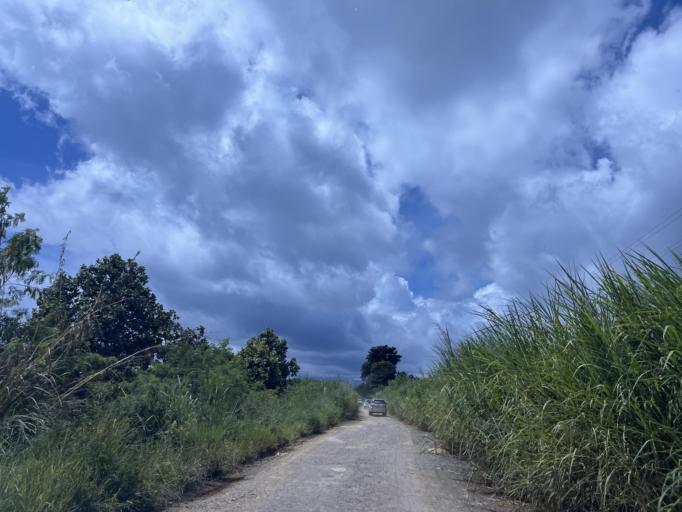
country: PH
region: Northern Mindanao
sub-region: Province of Bukidnon
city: Impalutao
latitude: 8.2486
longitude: 125.0008
